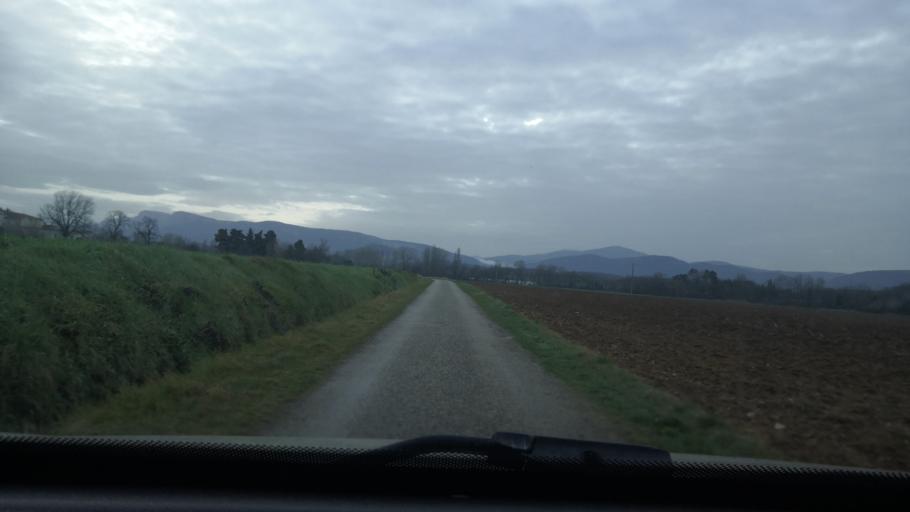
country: FR
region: Rhone-Alpes
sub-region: Departement de la Drome
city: La Begude-de-Mazenc
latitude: 44.5647
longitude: 4.8894
